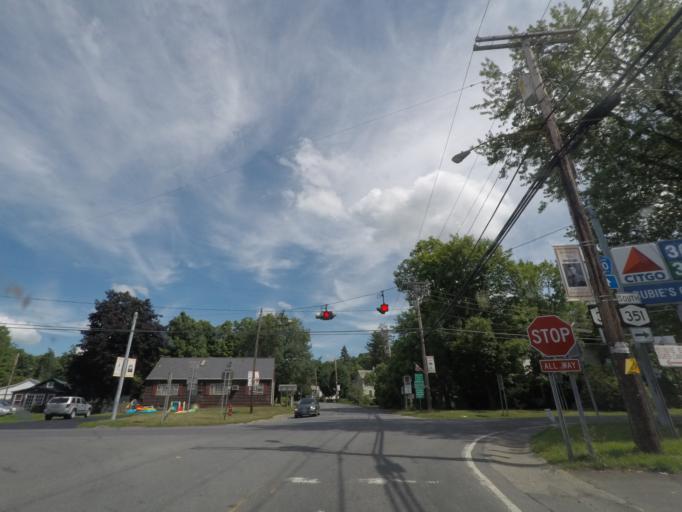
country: US
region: New York
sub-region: Rensselaer County
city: Poestenkill
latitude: 42.6903
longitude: -73.5646
